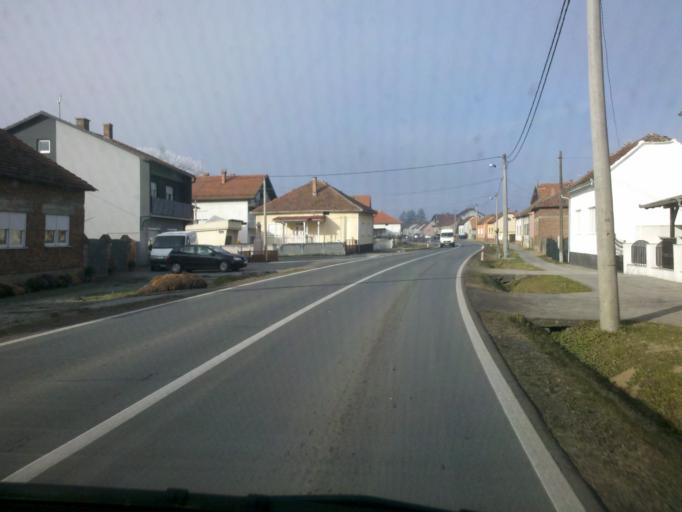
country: HR
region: Virovitick-Podravska
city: Pitomaca
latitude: 45.9581
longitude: 17.2253
